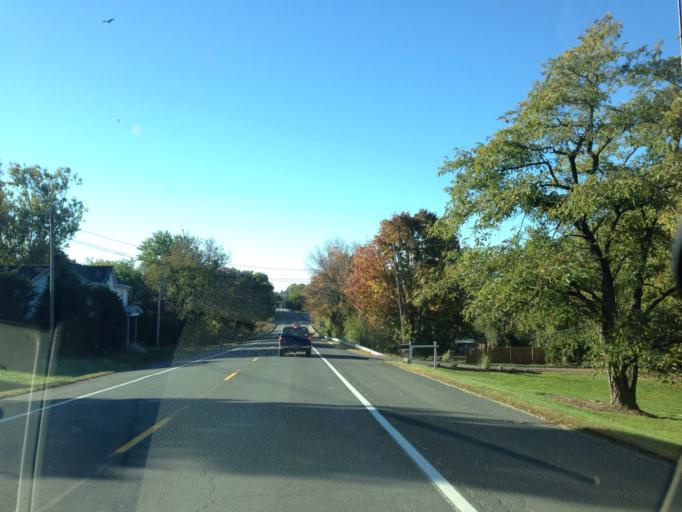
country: US
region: Maryland
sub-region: Montgomery County
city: Clarksburg
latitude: 39.2448
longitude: -77.2345
